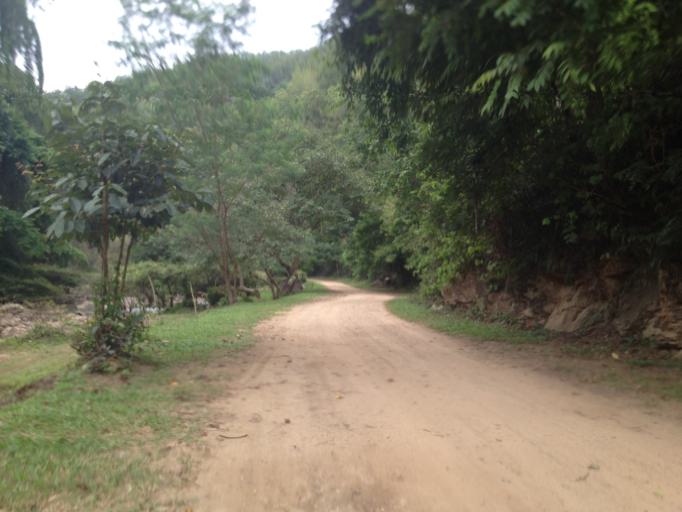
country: TH
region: Chiang Mai
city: Hang Dong
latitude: 18.7207
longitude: 98.8228
